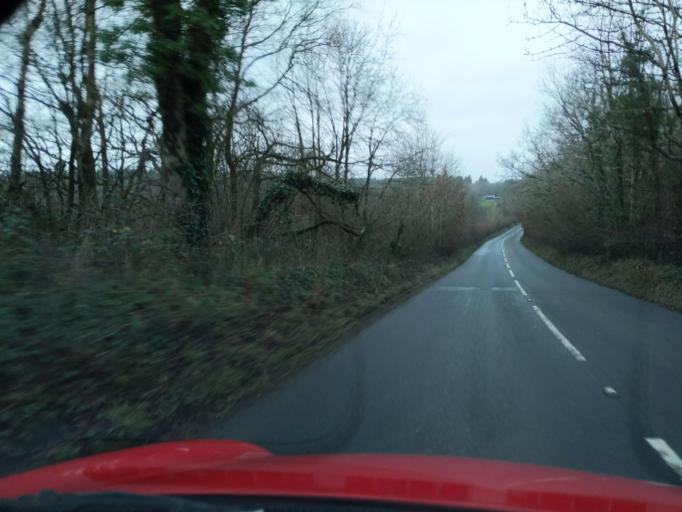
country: GB
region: England
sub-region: Devon
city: Holsworthy
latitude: 50.7816
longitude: -4.3357
